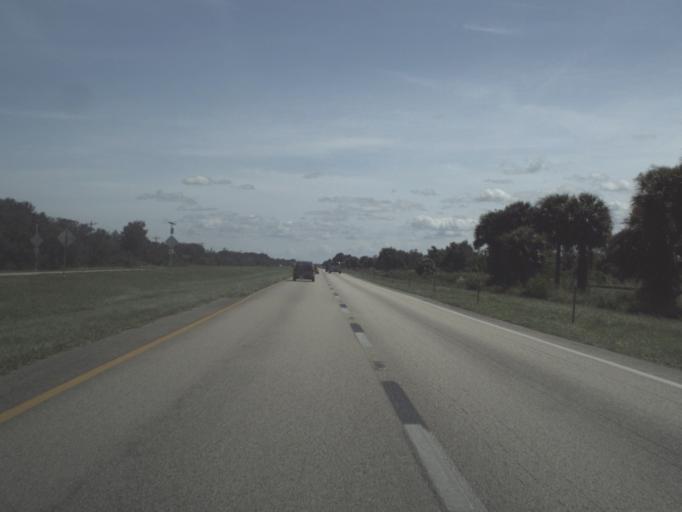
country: US
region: Florida
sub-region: Hendry County
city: Port LaBelle
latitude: 26.9244
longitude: -81.3105
